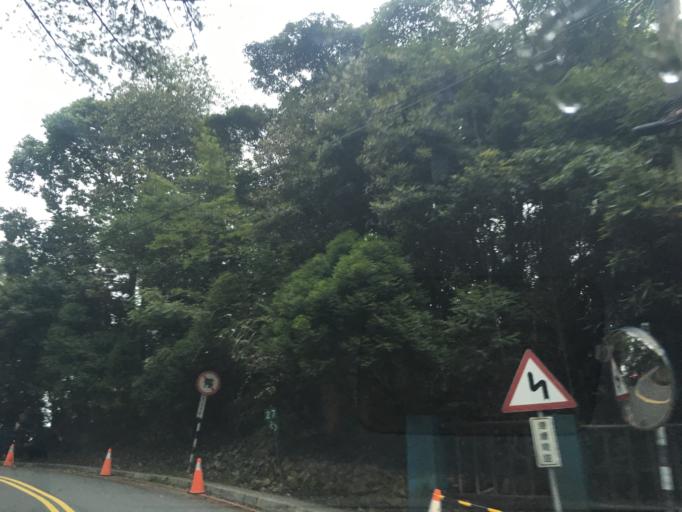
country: TW
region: Taiwan
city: Fengyuan
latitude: 24.2349
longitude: 120.9541
